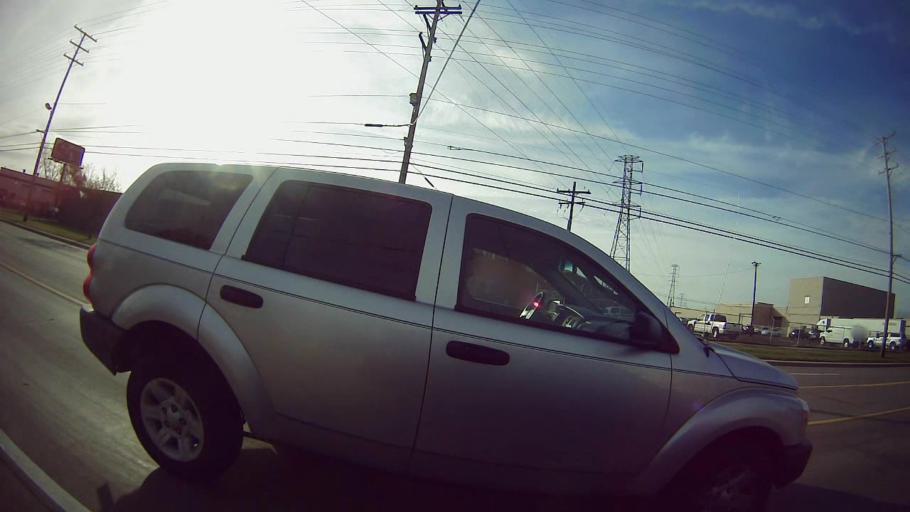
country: US
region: Michigan
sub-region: Macomb County
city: Warren
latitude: 42.4637
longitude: -82.9983
